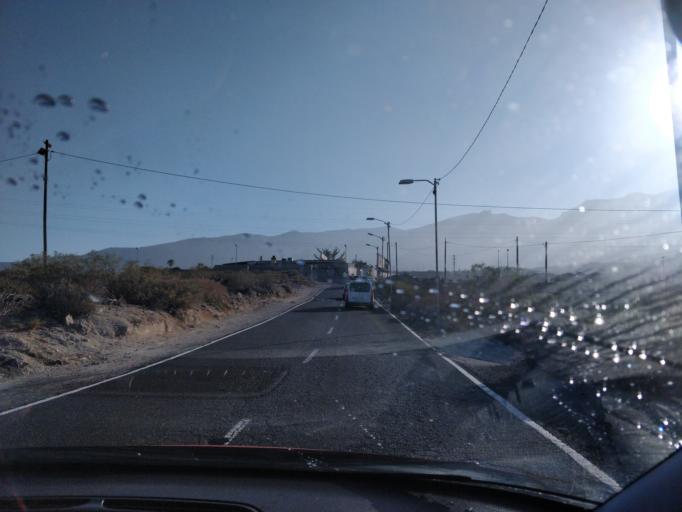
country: ES
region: Canary Islands
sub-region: Provincia de Santa Cruz de Tenerife
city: Candelaria
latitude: 28.3494
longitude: -16.3719
